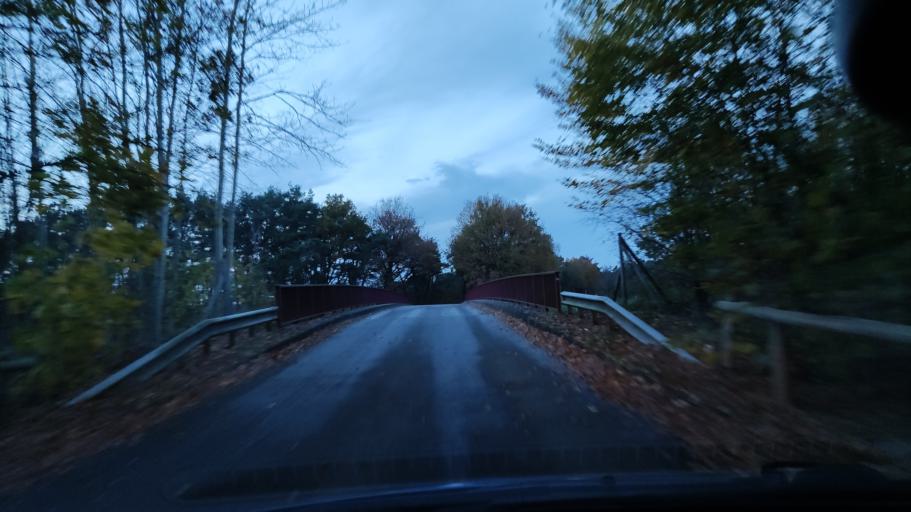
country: DE
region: Lower Saxony
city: Egestorf
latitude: 53.1495
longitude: 10.0326
